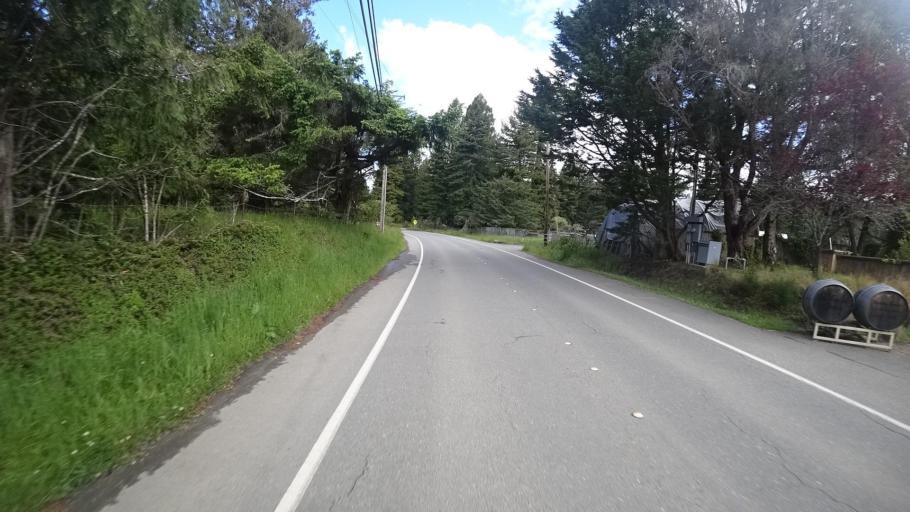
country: US
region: California
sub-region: Humboldt County
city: McKinleyville
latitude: 40.9591
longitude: -124.0337
